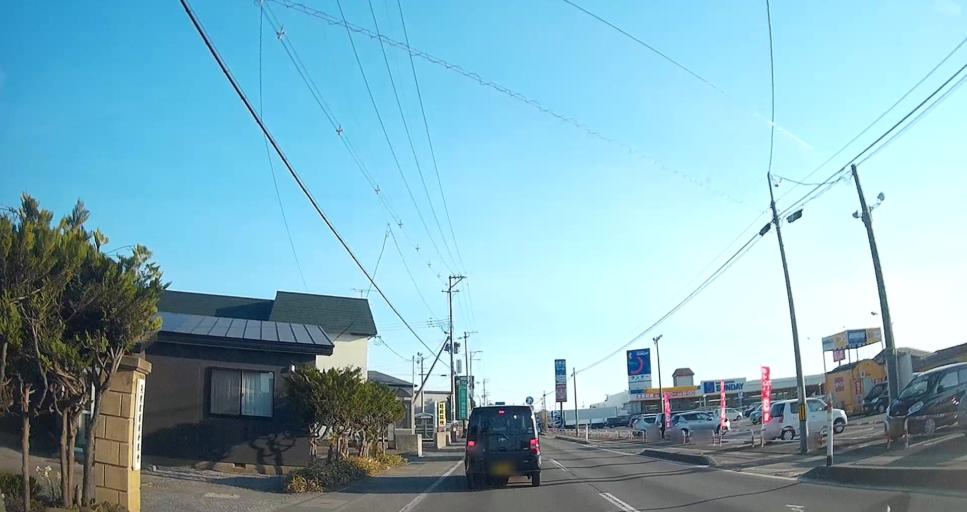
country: JP
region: Aomori
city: Mutsu
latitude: 41.2857
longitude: 141.2114
